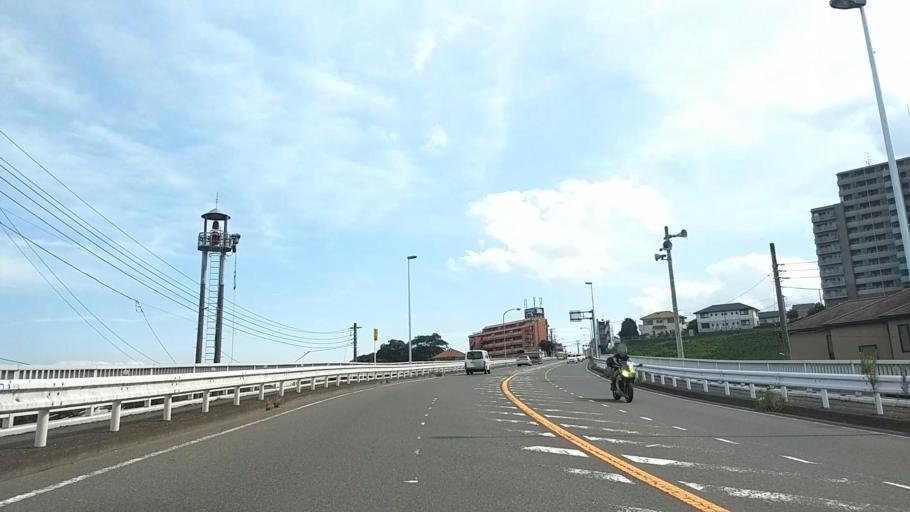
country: JP
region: Kanagawa
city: Yokohama
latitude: 35.5141
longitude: 139.5840
